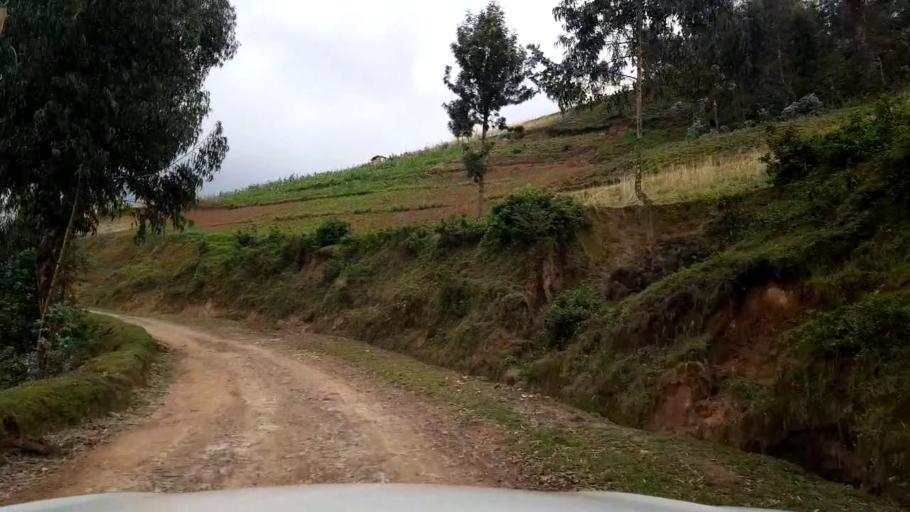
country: RW
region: Western Province
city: Kibuye
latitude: -1.9670
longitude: 29.4853
